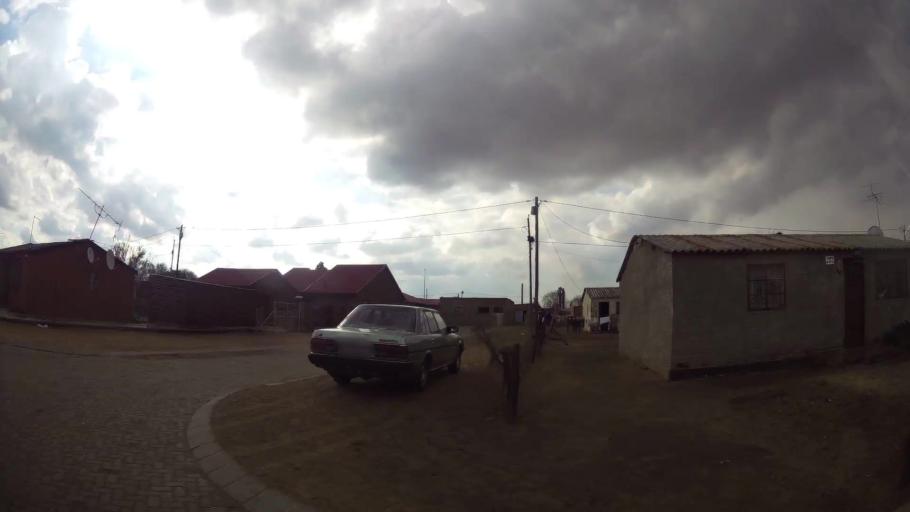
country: ZA
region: Orange Free State
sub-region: Fezile Dabi District Municipality
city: Sasolburg
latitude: -26.8405
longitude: 27.8494
